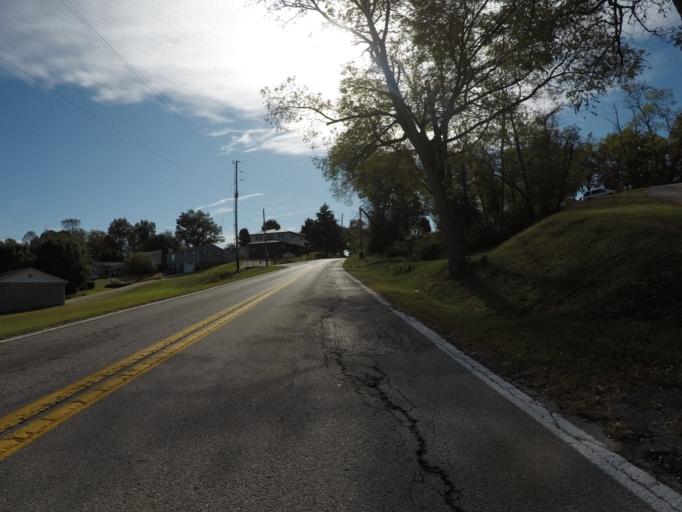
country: US
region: Ohio
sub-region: Lawrence County
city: Burlington
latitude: 38.3590
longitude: -82.5253
